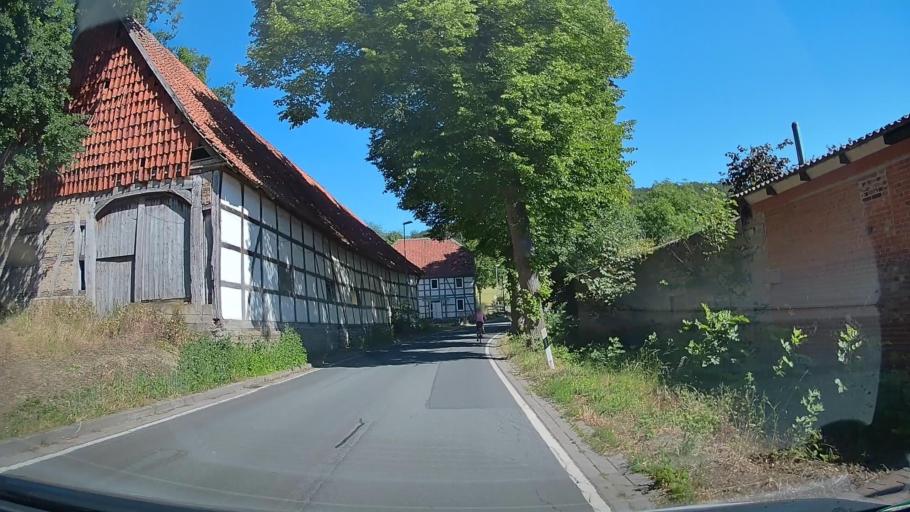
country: DE
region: Lower Saxony
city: Vahlbruch
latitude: 51.9845
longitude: 9.3489
